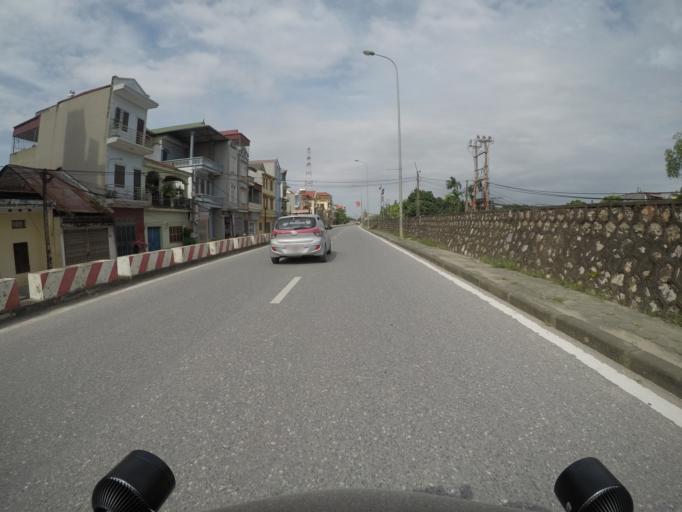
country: VN
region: Ha Noi
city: Tay Ho
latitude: 21.0924
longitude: 105.7816
